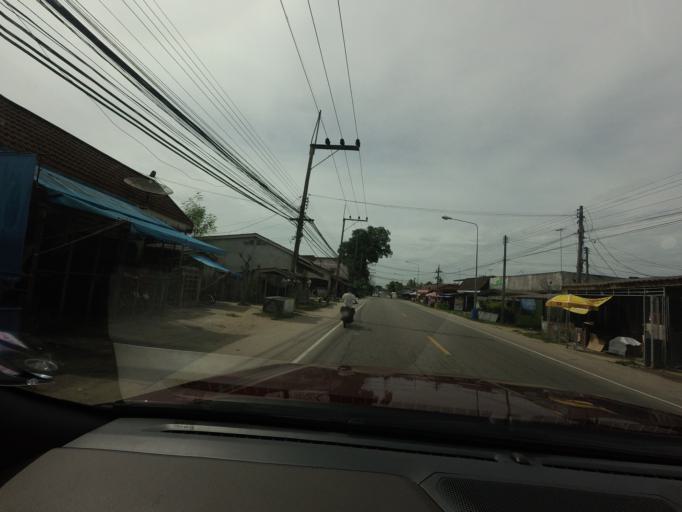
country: TH
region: Narathiwat
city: Tak Bai
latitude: 6.2541
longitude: 102.0614
